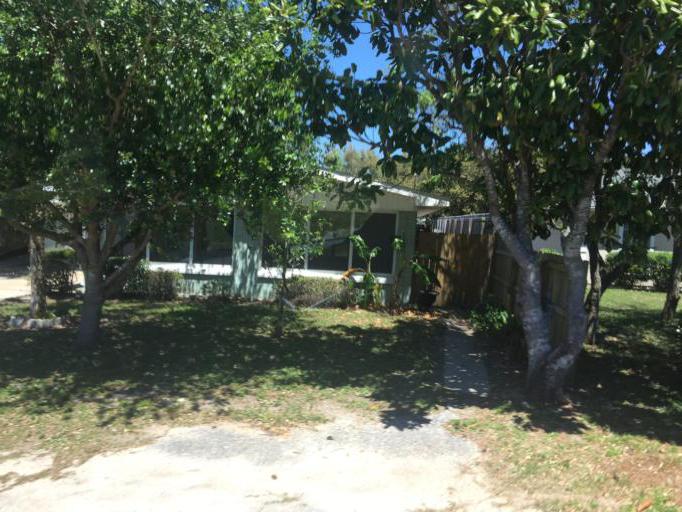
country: US
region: Florida
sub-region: Bay County
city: Laguna Beach
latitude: 30.2599
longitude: -85.9690
